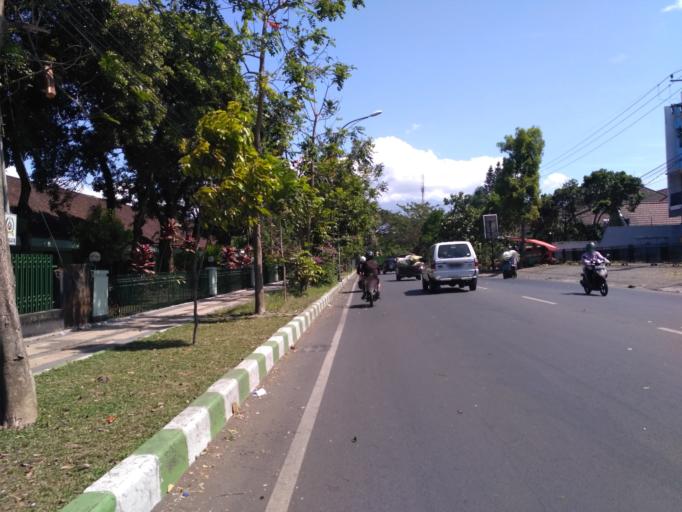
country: ID
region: East Java
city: Malang
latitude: -7.9788
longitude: 112.6471
